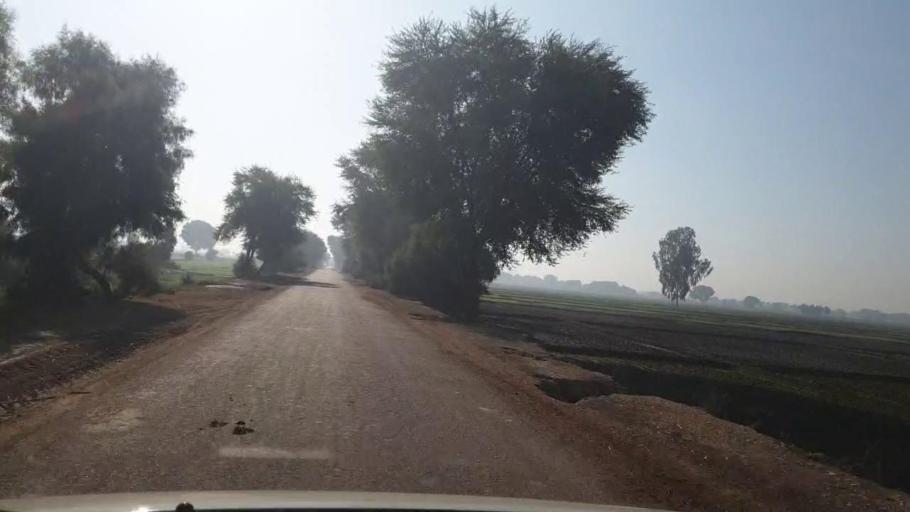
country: PK
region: Sindh
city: Dadu
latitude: 26.6636
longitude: 67.8182
